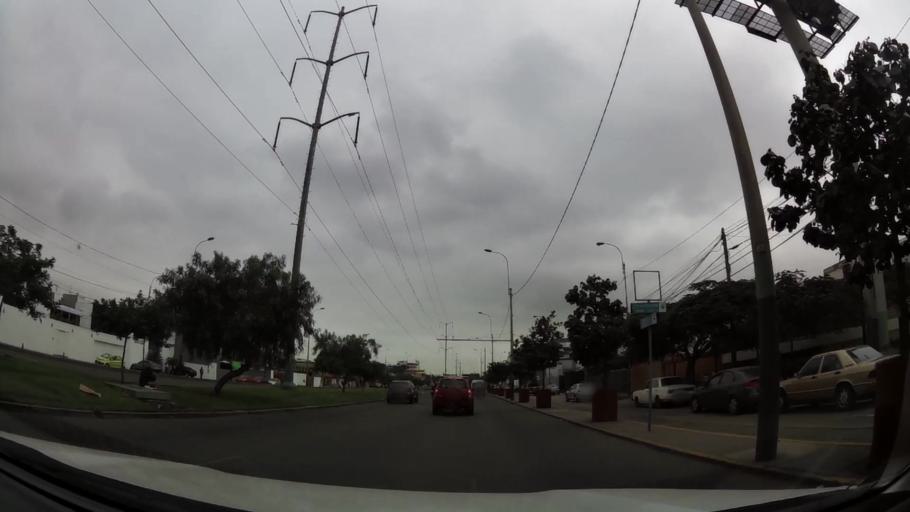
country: PE
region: Lima
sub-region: Lima
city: San Luis
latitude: -12.1104
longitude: -76.9831
